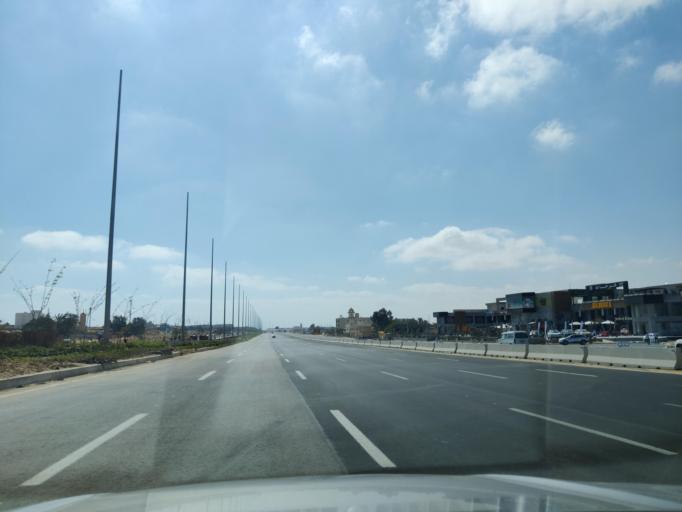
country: EG
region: Muhafazat Matruh
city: Al `Alamayn
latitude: 30.9909
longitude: 28.6805
